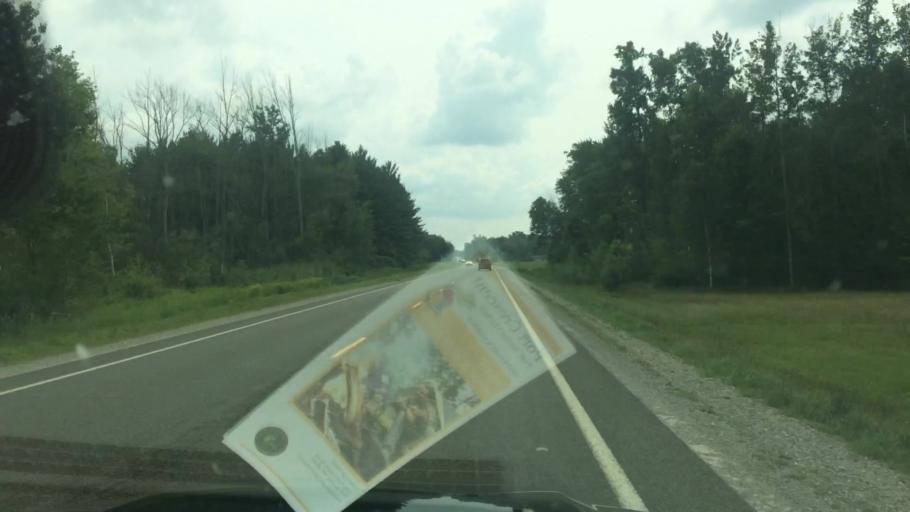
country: US
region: Michigan
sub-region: Tuscola County
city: Cass City
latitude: 43.6508
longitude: -83.0983
